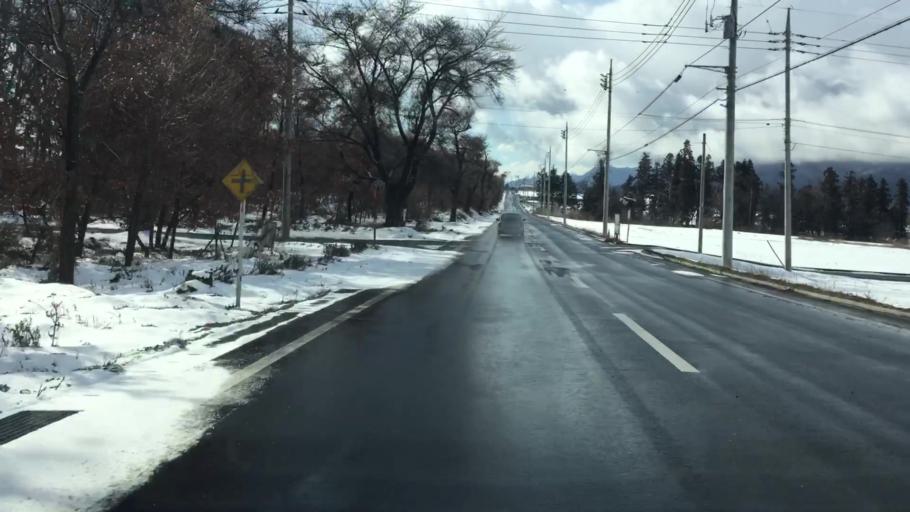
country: JP
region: Gunma
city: Numata
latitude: 36.6194
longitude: 139.0856
